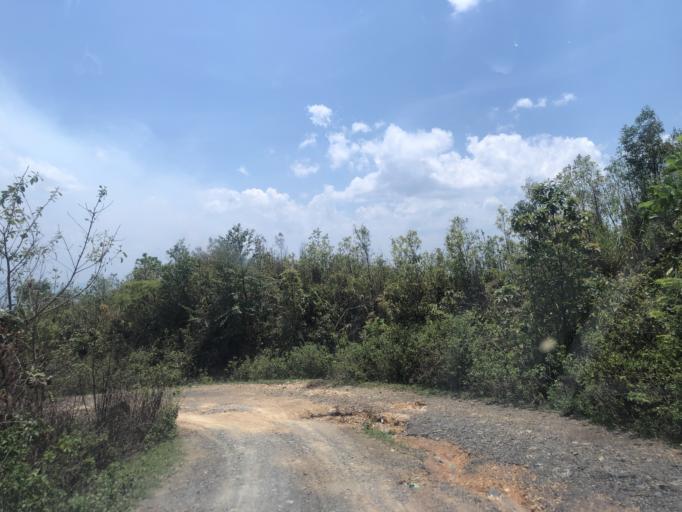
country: LA
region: Phongsali
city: Phongsali
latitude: 21.4333
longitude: 102.1623
